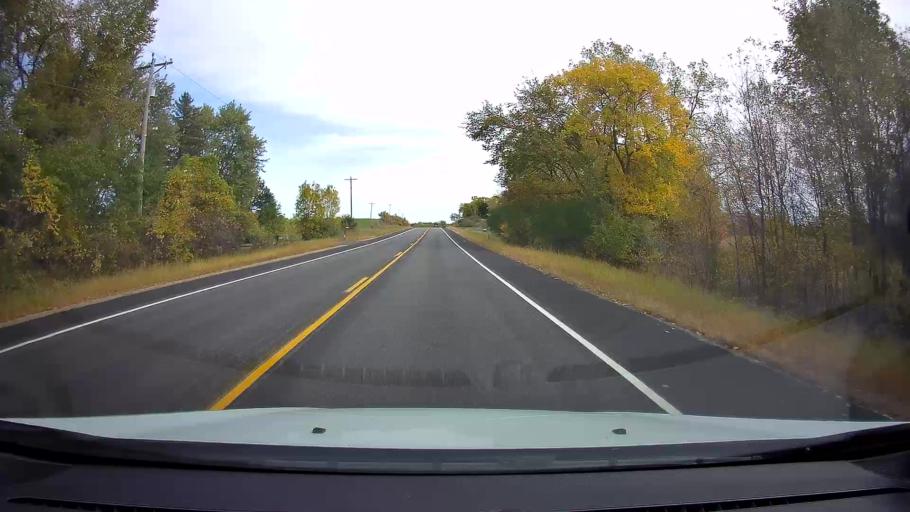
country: US
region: Minnesota
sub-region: Washington County
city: Stillwater
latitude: 45.1181
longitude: -92.7724
